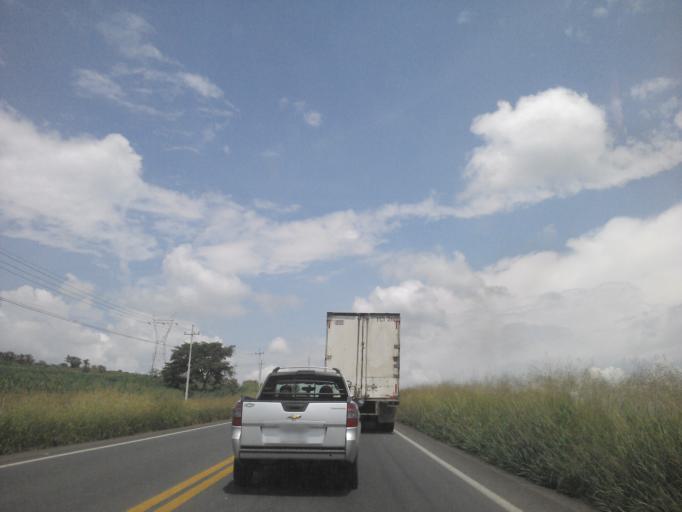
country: MX
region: Jalisco
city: Acatic
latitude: 20.6972
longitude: -102.9765
